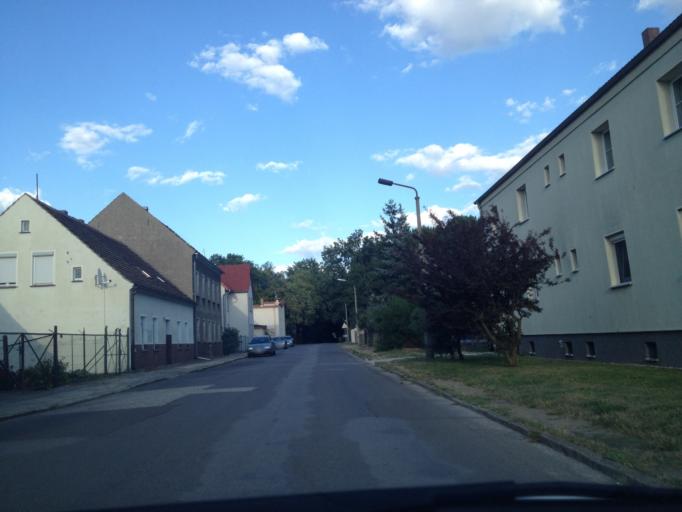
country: DE
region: Brandenburg
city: Vetschau
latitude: 51.7893
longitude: 14.0748
